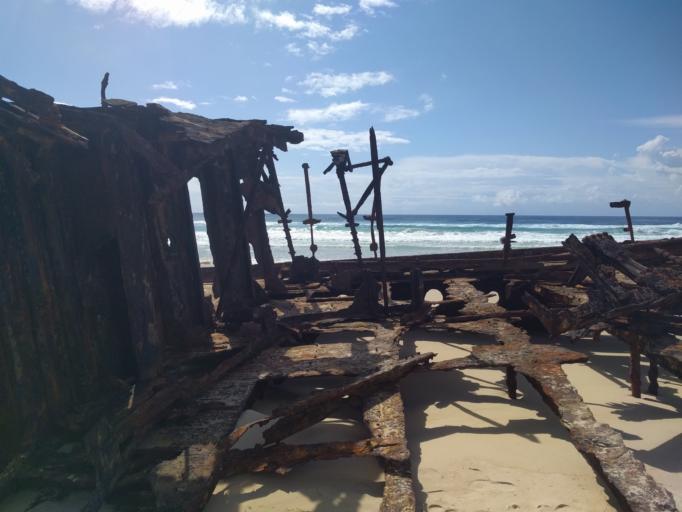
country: AU
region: Queensland
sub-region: Fraser Coast
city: Urangan
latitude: -25.2676
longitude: 153.2382
